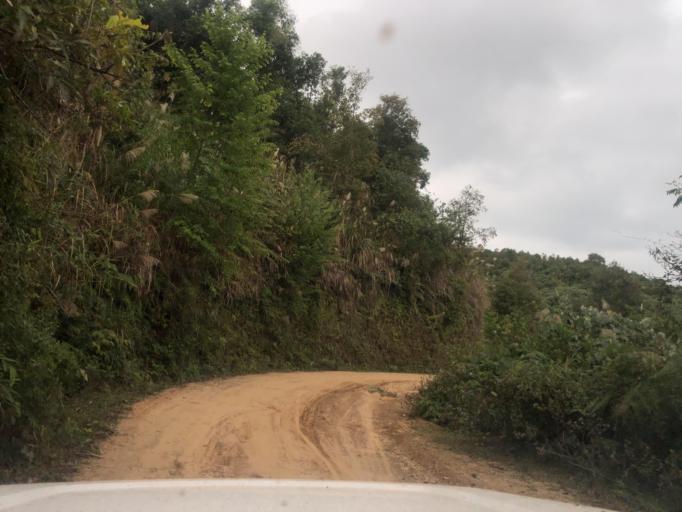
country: LA
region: Phongsali
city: Khoa
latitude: 21.2659
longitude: 102.5889
